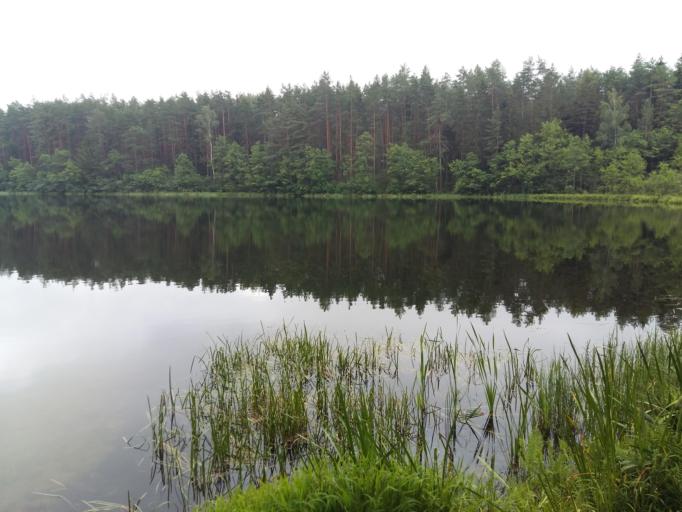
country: LT
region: Alytaus apskritis
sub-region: Alytus
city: Alytus
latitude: 54.1895
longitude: 24.1453
